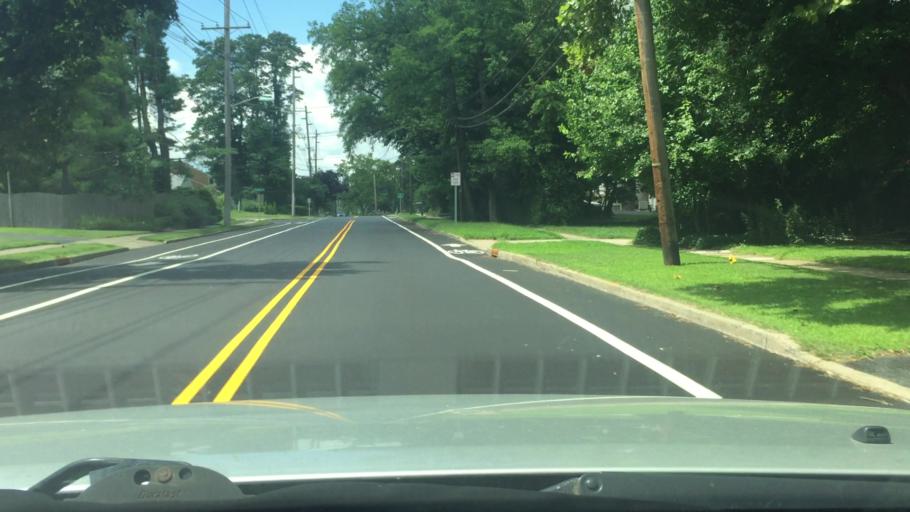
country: US
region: New Jersey
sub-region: Middlesex County
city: East Brunswick
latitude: 40.4253
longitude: -74.4180
